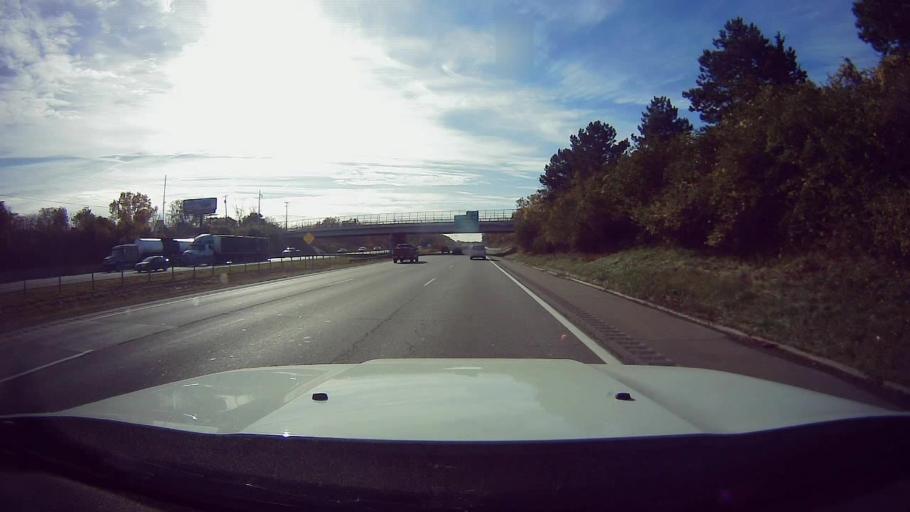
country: US
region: Michigan
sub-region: Wayne County
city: Plymouth
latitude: 42.3738
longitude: -83.4368
